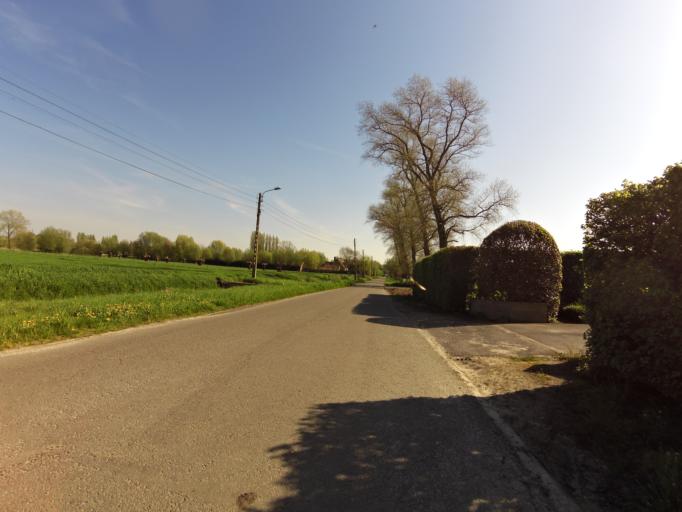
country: BE
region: Flanders
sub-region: Provincie West-Vlaanderen
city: Oudenburg
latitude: 51.1819
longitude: 3.0404
